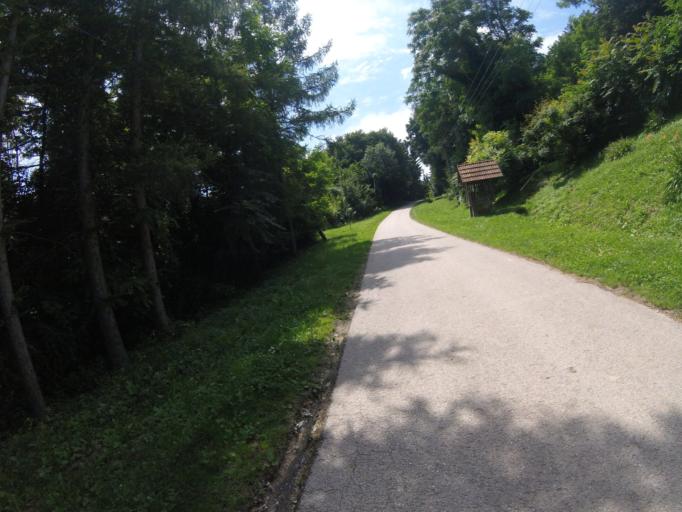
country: HU
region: Zala
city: Nagykanizsa
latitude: 46.5506
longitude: 17.0379
